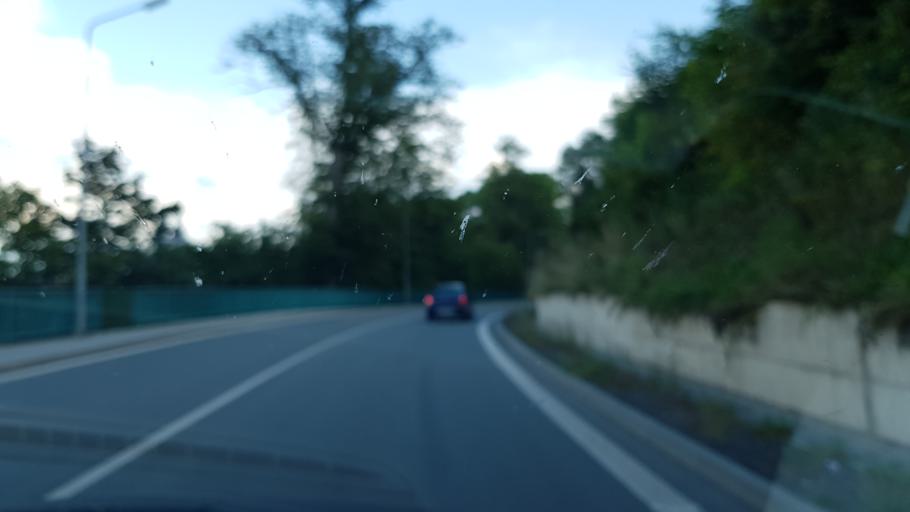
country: CZ
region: Pardubicky
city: Zamberk
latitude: 50.0882
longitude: 16.4576
